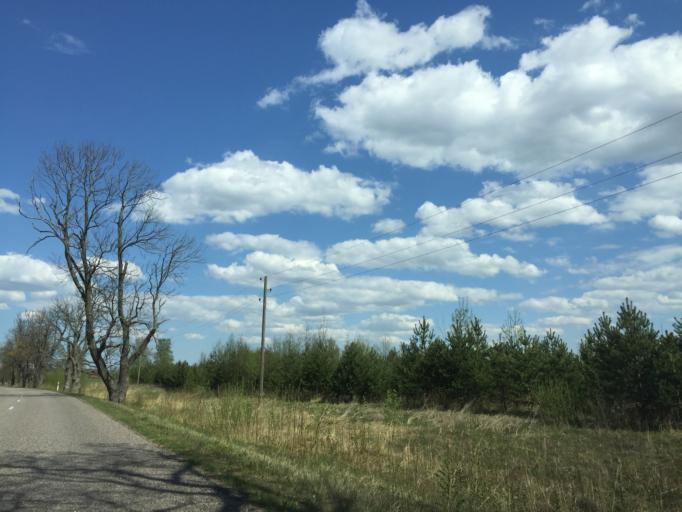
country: LV
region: Saulkrastu
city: Saulkrasti
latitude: 57.3605
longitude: 24.4868
